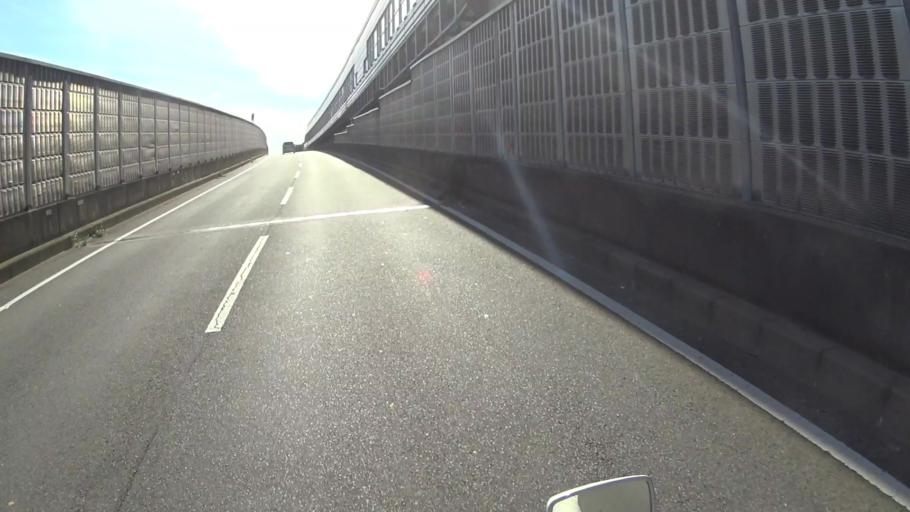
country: JP
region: Kyoto
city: Uji
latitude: 34.9066
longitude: 135.7760
